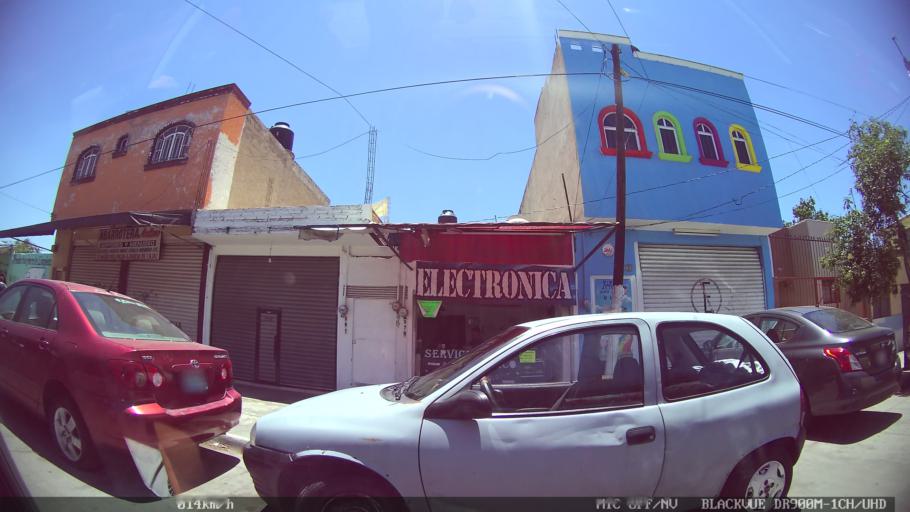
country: MX
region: Jalisco
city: Tlaquepaque
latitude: 20.6691
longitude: -103.2760
